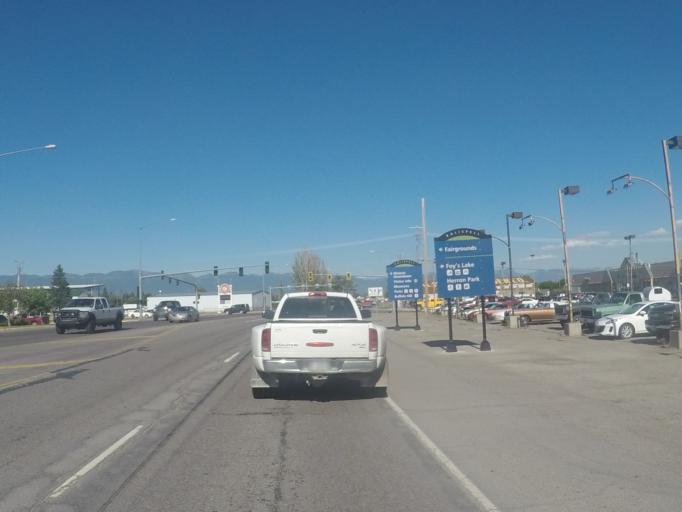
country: US
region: Montana
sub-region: Flathead County
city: Kalispell
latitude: 48.2004
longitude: -114.3316
